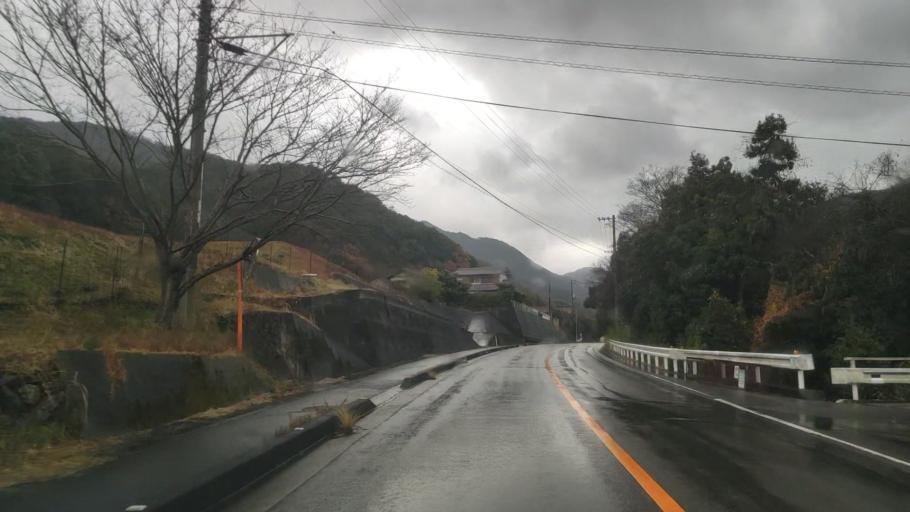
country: JP
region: Tokushima
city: Kamojimacho-jogejima
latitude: 34.1968
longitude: 134.3322
